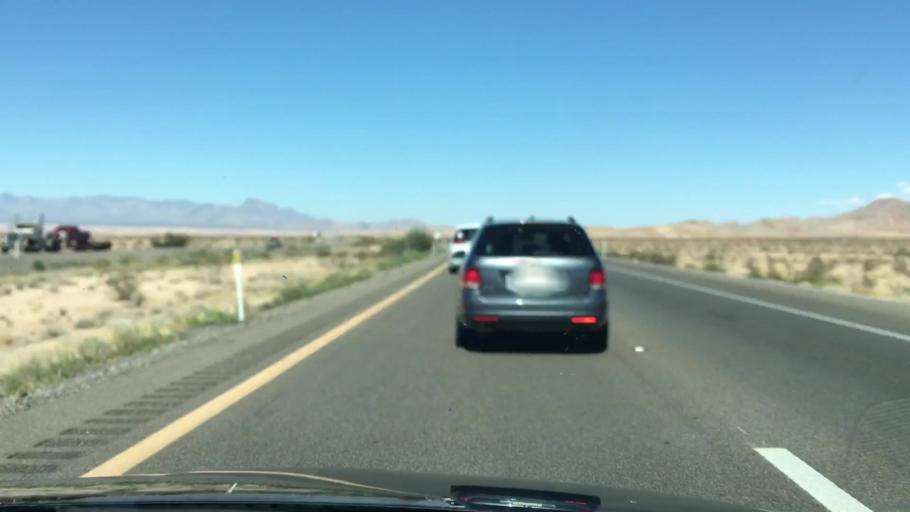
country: US
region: Nevada
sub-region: Clark County
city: Moapa Town
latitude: 36.5802
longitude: -114.6560
